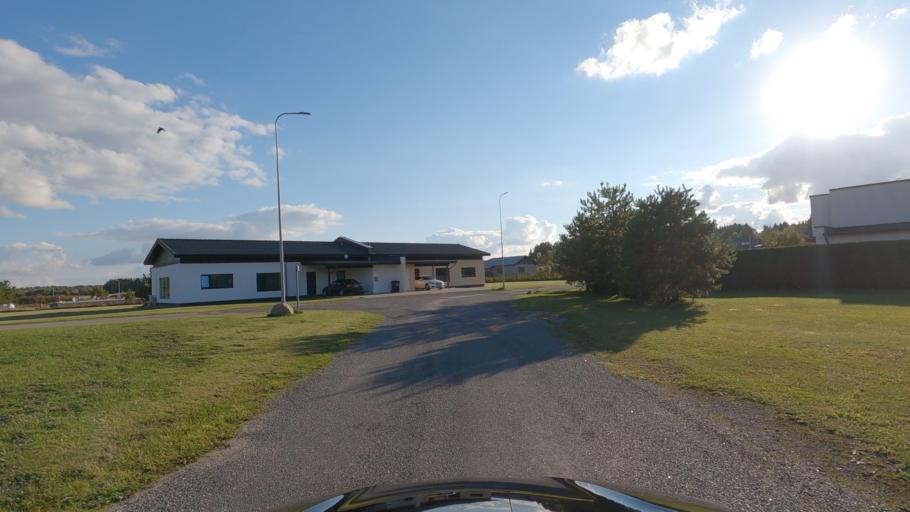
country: EE
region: Harju
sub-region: Saue vald
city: Laagri
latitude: 59.3425
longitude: 24.6522
